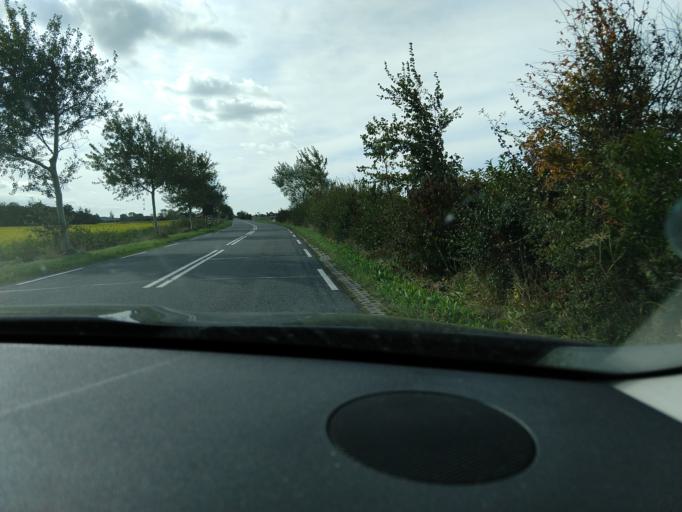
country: NL
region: Zeeland
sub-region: Gemeente Middelburg
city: Middelburg
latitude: 51.5253
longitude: 3.5400
